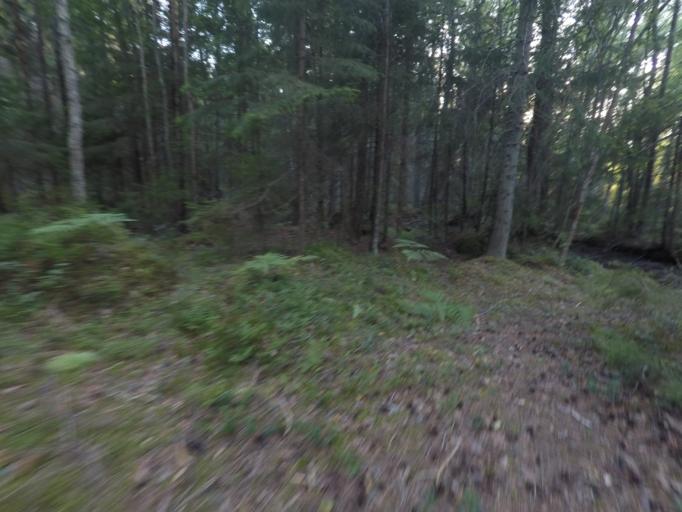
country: SE
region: Soedermanland
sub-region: Eskilstuna Kommun
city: Kvicksund
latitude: 59.4147
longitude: 16.3204
